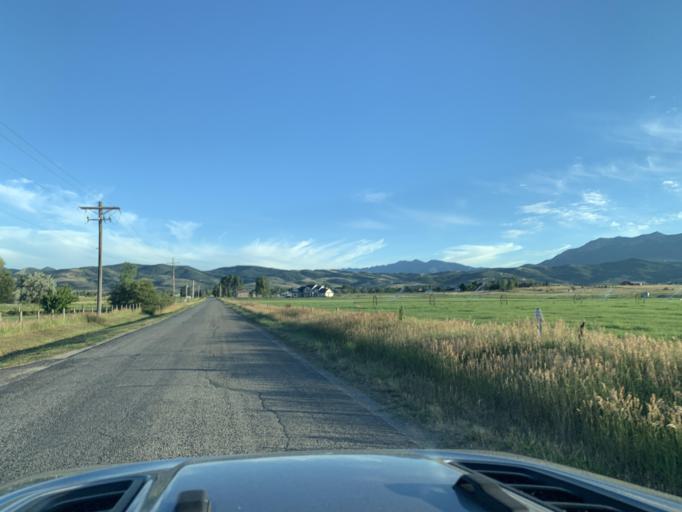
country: US
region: Utah
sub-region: Weber County
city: Wolf Creek
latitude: 41.2759
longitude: -111.7620
